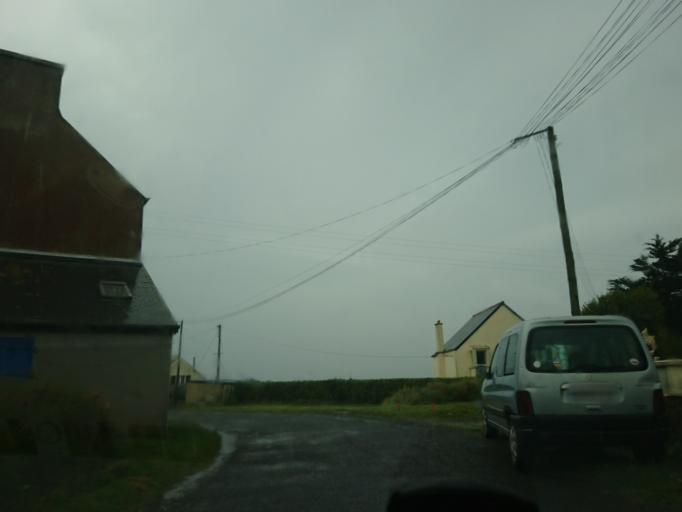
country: FR
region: Brittany
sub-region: Departement du Finistere
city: Guisseny
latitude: 48.6383
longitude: -4.4413
